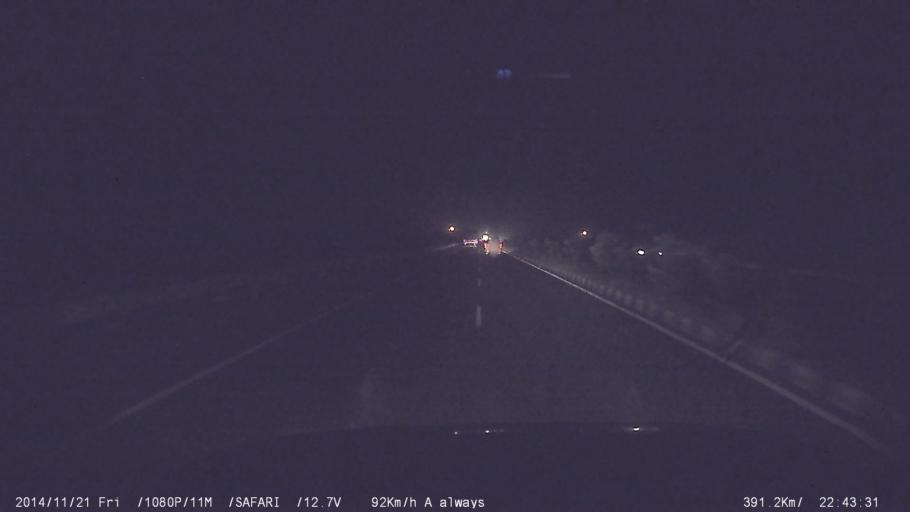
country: IN
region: Tamil Nadu
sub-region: Villupuram
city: Tindivanam
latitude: 12.2273
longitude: 79.6649
